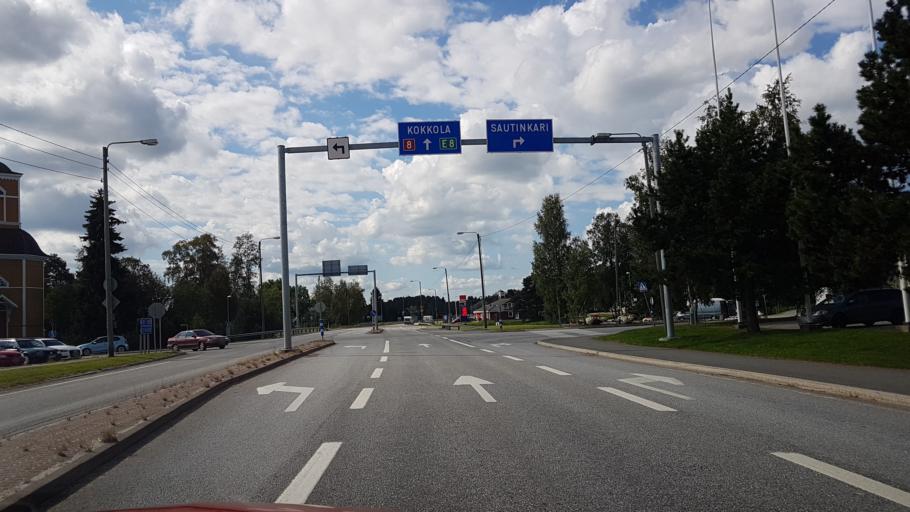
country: FI
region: Northern Ostrobothnia
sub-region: Ylivieska
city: Himanka
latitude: 64.0620
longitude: 23.6550
